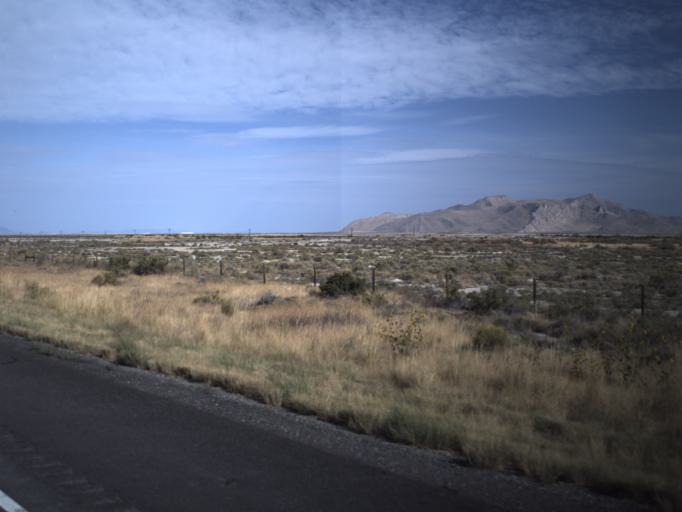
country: US
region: Utah
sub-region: Tooele County
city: Grantsville
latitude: 40.6903
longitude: -112.4600
